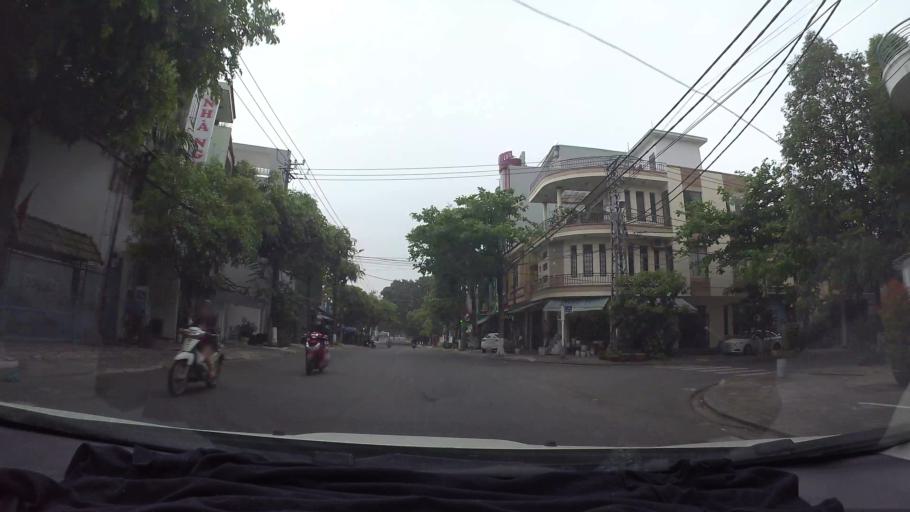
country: VN
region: Da Nang
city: Cam Le
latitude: 16.0288
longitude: 108.2222
